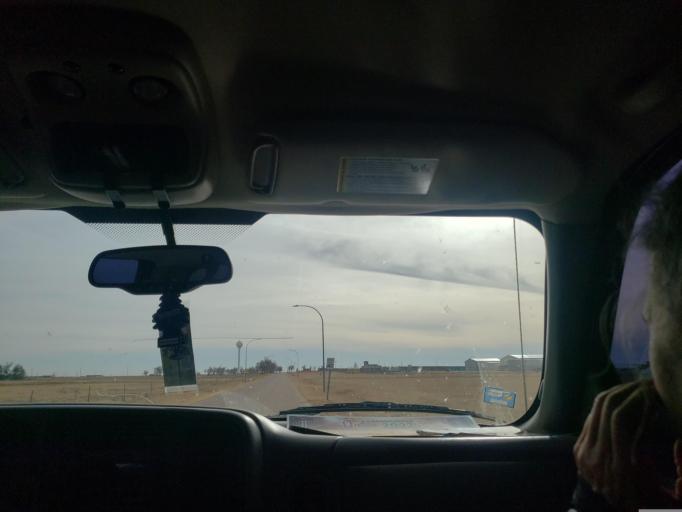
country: US
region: Kansas
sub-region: Finney County
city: Garden City
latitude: 37.9362
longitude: -100.7182
